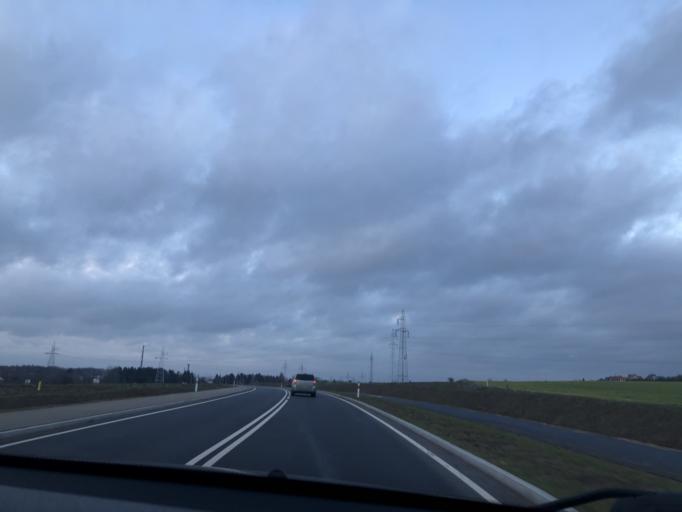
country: PL
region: Podlasie
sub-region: Lomza
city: Lomza
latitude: 53.1465
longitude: 22.0528
